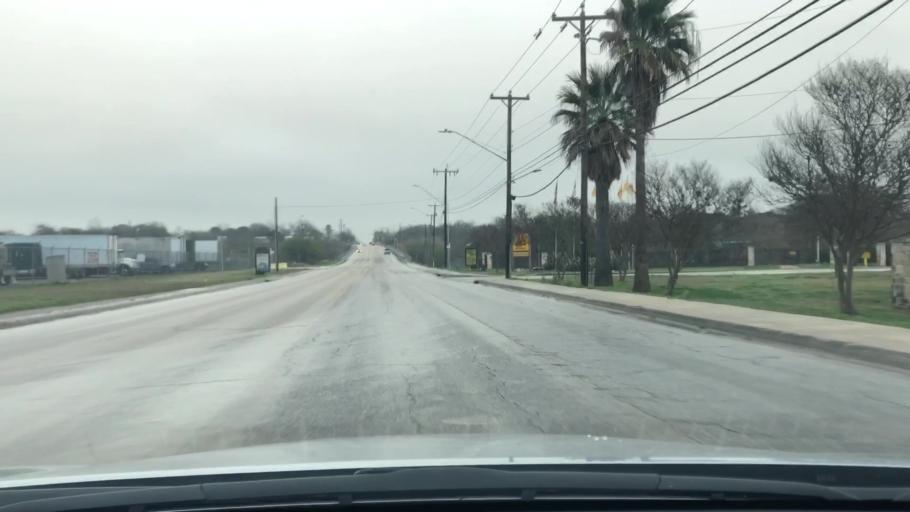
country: US
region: Texas
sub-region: Bexar County
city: Kirby
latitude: 29.4357
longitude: -98.4227
